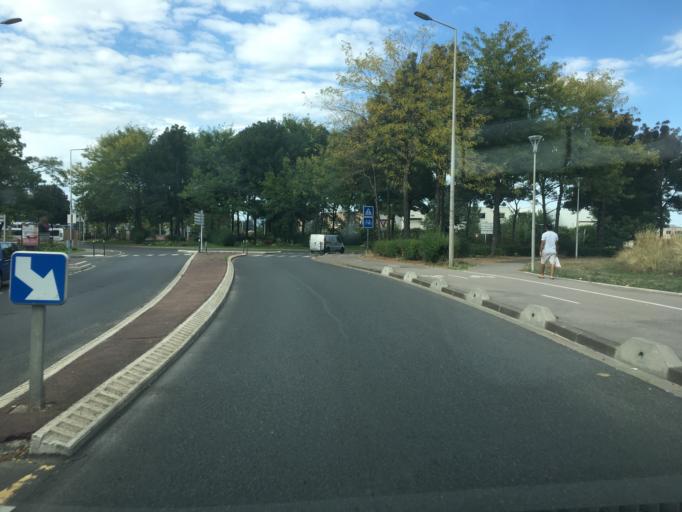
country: FR
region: Ile-de-France
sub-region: Departement du Val-de-Marne
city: Valenton
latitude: 48.7516
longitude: 2.4549
